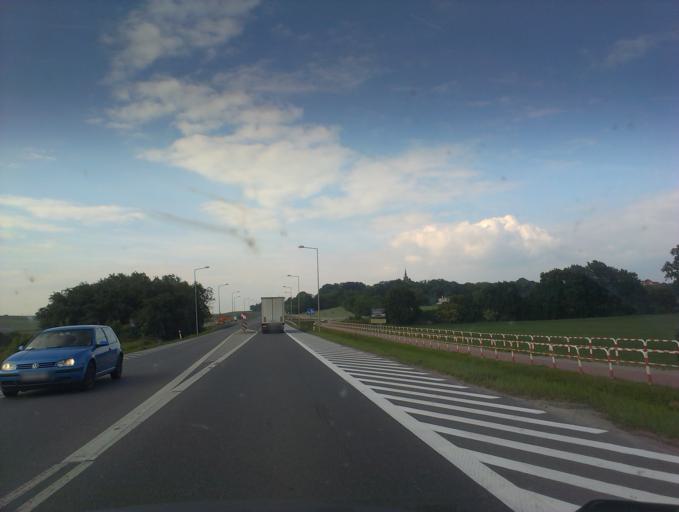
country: PL
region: Lower Silesian Voivodeship
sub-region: Powiat trzebnicki
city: Trzebnica
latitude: 51.2607
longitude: 17.0474
